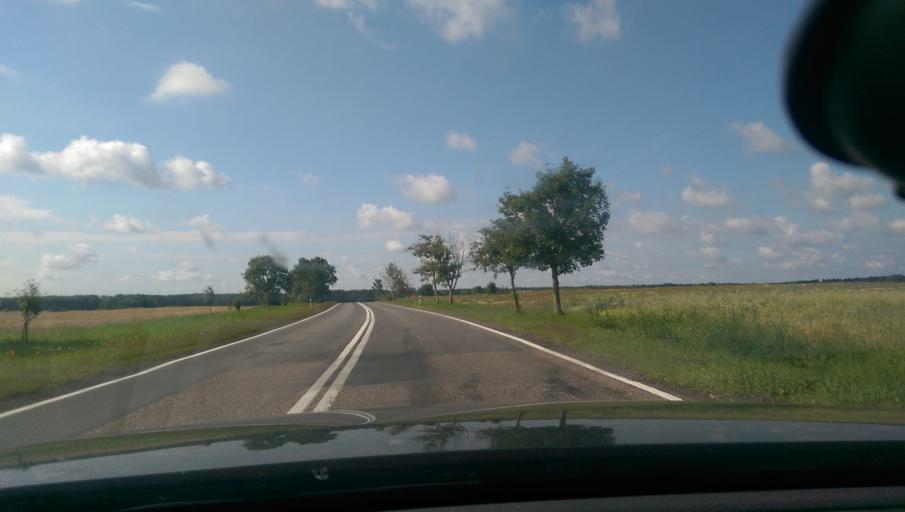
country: PL
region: West Pomeranian Voivodeship
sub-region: Powiat walecki
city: Walcz
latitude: 53.3356
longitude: 16.5645
